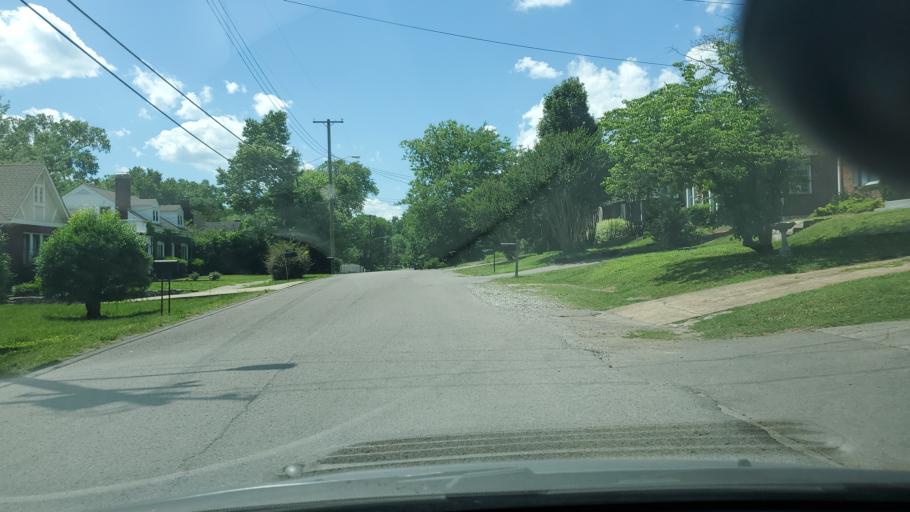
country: US
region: Tennessee
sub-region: Davidson County
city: Nashville
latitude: 36.2021
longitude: -86.7431
